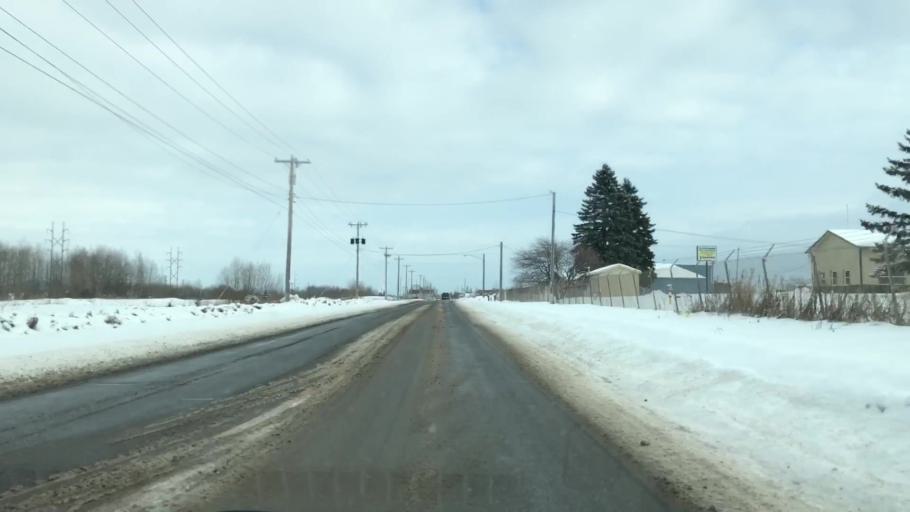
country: US
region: Wisconsin
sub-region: Douglas County
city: Superior
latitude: 46.7280
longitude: -92.1226
